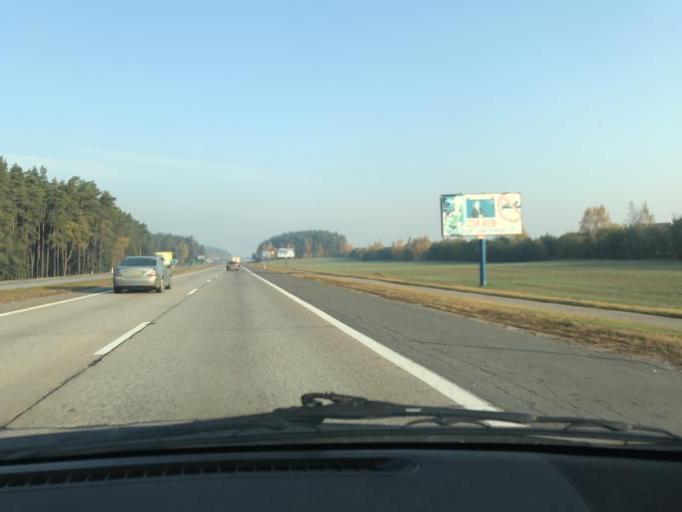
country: BY
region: Minsk
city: Borovlyany
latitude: 53.9955
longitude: 27.6572
